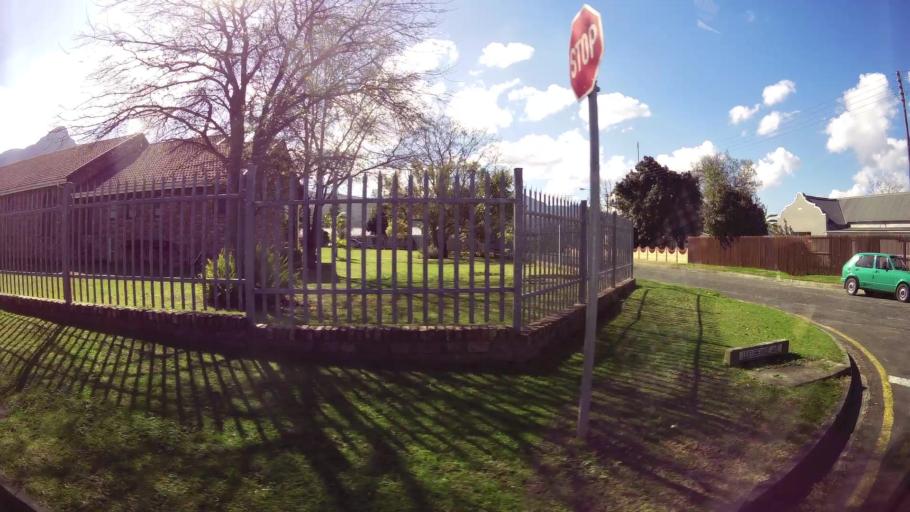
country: ZA
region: Western Cape
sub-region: Eden District Municipality
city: George
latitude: -33.9504
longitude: 22.4754
